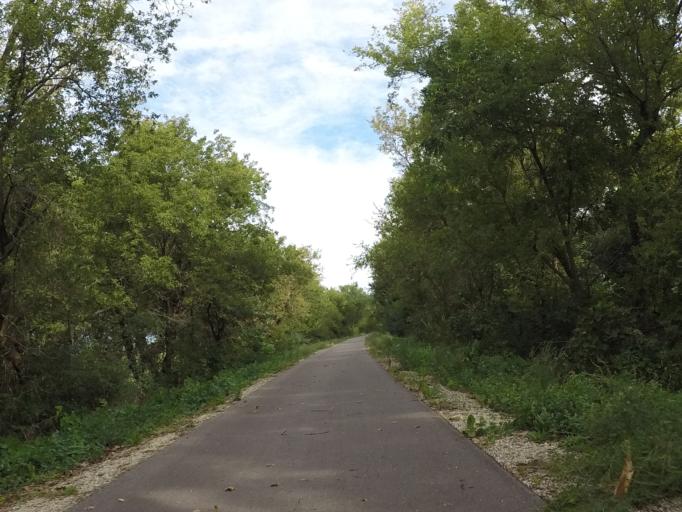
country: US
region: Wisconsin
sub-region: Sauk County
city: Prairie du Sac
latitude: 43.3303
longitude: -89.7499
